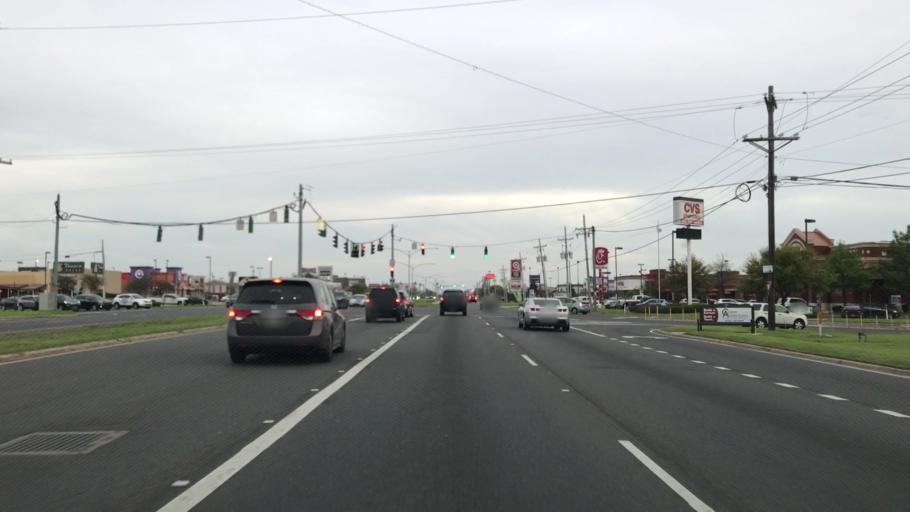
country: US
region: Louisiana
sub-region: Bossier Parish
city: Bossier City
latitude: 32.4440
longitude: -93.7191
